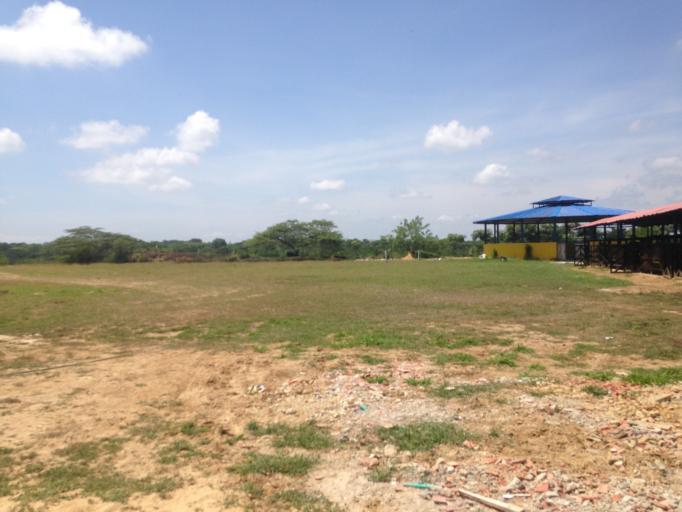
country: CO
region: Atlantico
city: Baranoa
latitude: 10.8422
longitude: -74.9051
